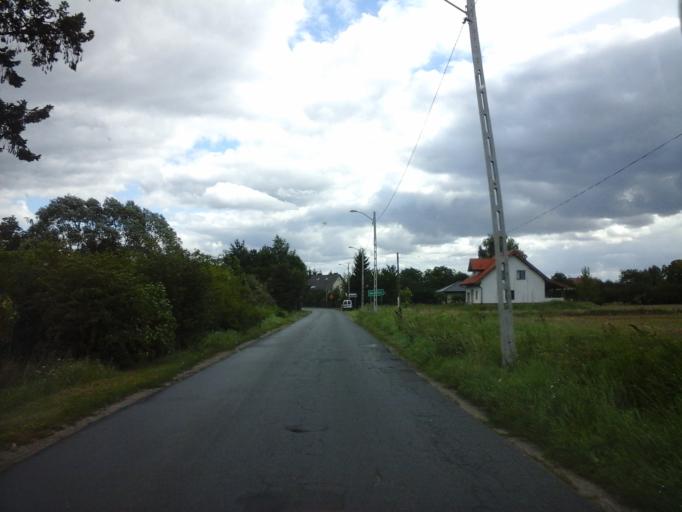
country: PL
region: West Pomeranian Voivodeship
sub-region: Powiat policki
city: Przeclaw
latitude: 53.3876
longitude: 14.4515
